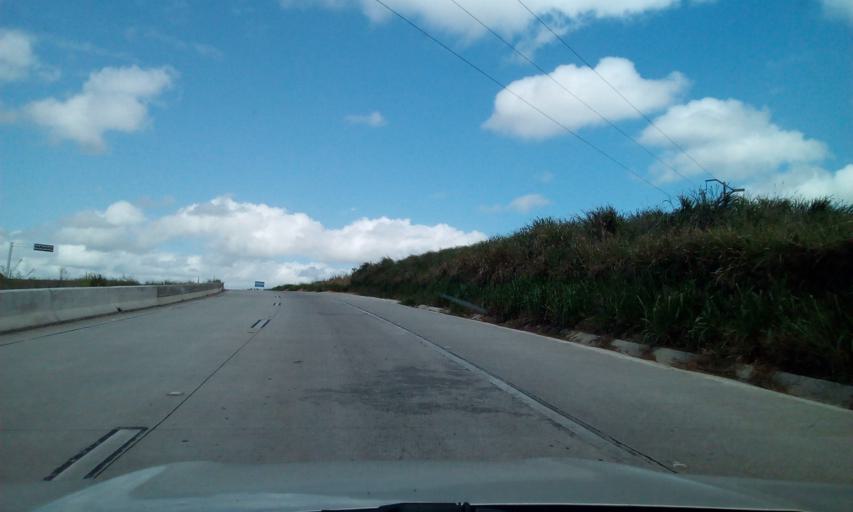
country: BR
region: Alagoas
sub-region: Rio Largo
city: Rio Largo
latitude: -9.4824
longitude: -35.8882
